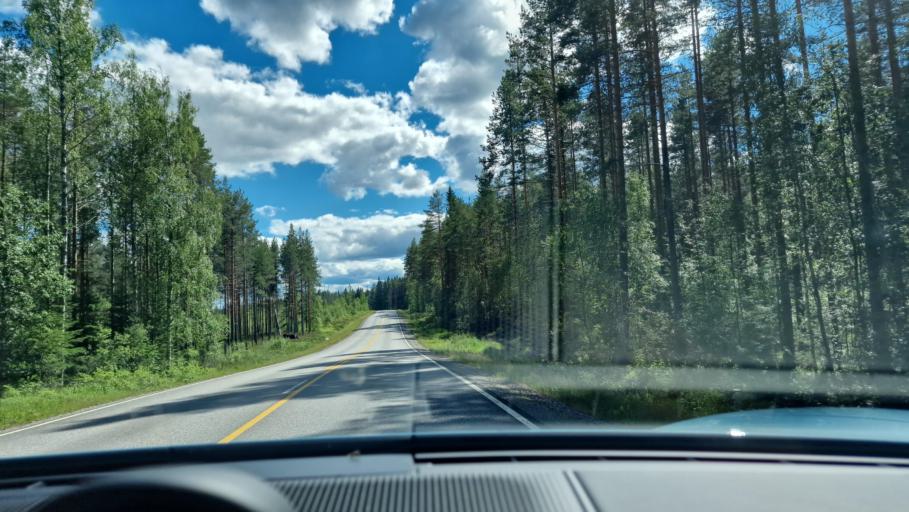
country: FI
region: Central Finland
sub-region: Saarijaervi-Viitasaari
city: Pylkoenmaeki
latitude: 62.6516
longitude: 24.5723
